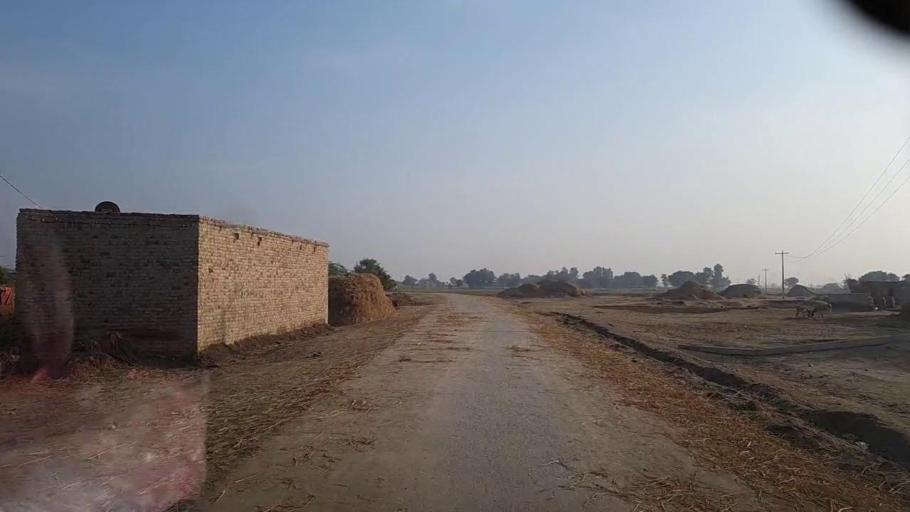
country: PK
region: Sindh
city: Jacobabad
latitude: 28.2359
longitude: 68.4847
